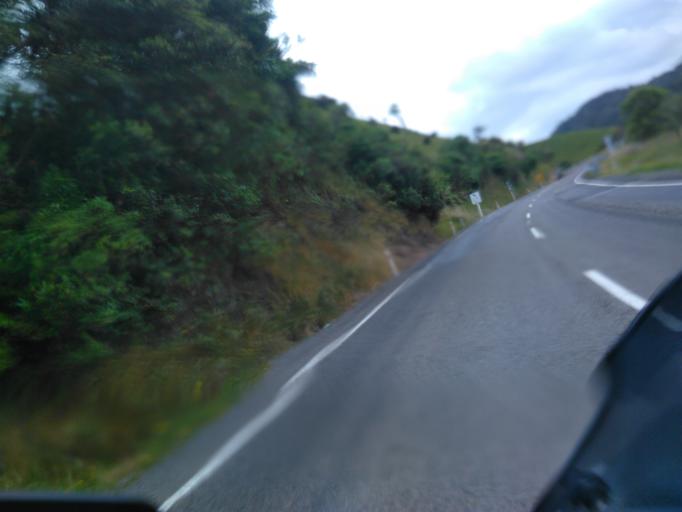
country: NZ
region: Bay of Plenty
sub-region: Opotiki District
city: Opotiki
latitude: -38.3497
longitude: 177.4491
